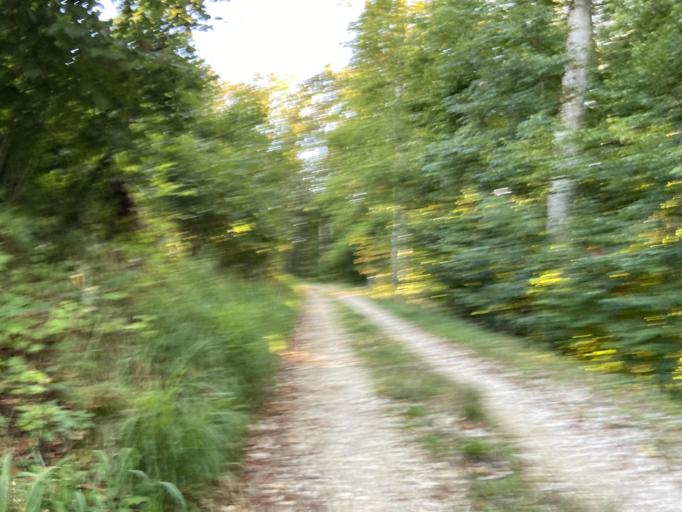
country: DE
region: Baden-Wuerttemberg
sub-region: Tuebingen Region
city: Bingen
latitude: 48.1212
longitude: 9.2966
